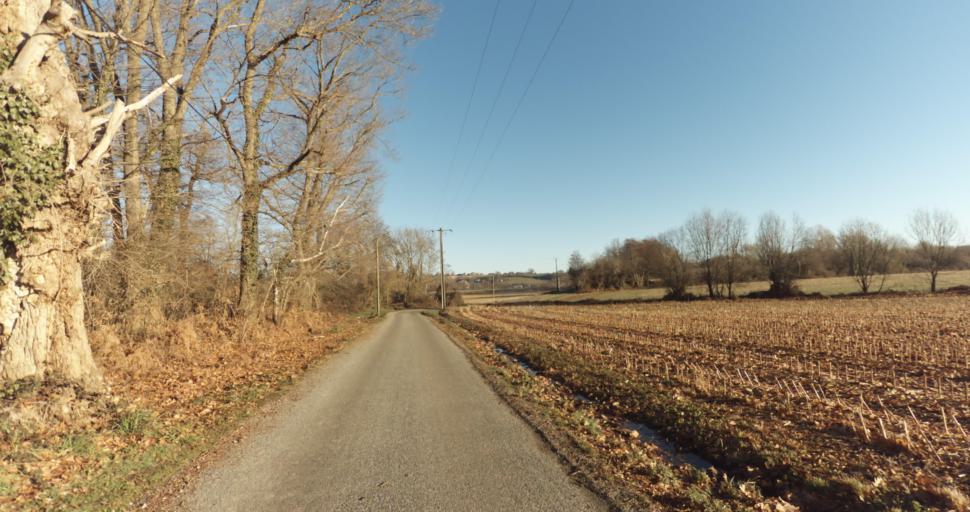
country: FR
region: Aquitaine
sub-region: Departement des Pyrenees-Atlantiques
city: Ousse
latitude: 43.3095
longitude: -0.2612
